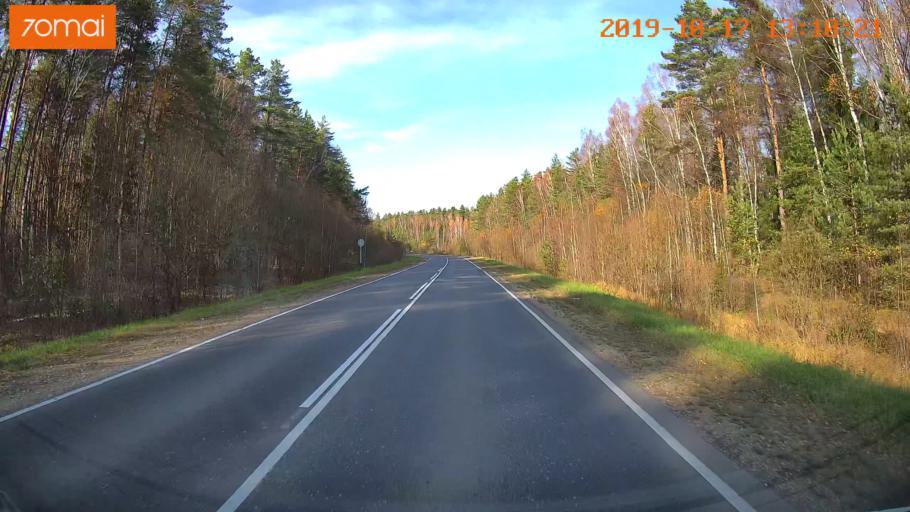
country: RU
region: Rjazan
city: Syntul
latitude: 55.0174
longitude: 41.2572
